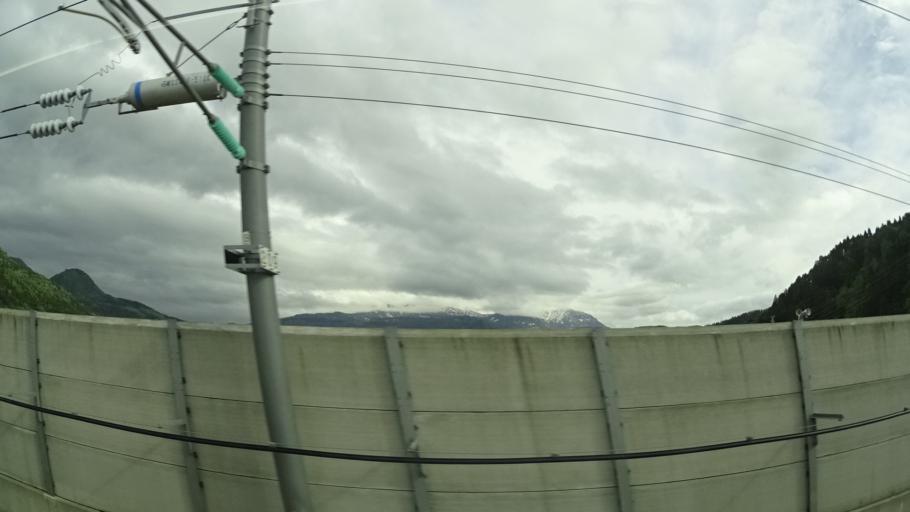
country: JP
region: Niigata
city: Itoigawa
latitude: 37.0541
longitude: 137.9129
